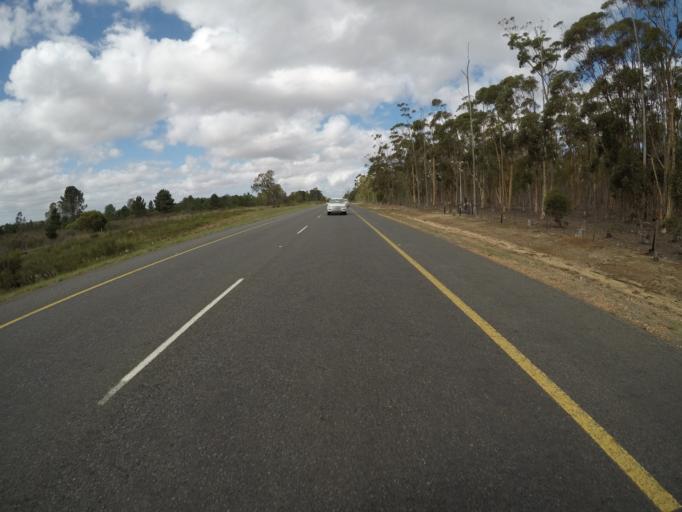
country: ZA
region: Western Cape
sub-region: Eden District Municipality
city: Riversdale
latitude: -34.1856
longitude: 21.4327
